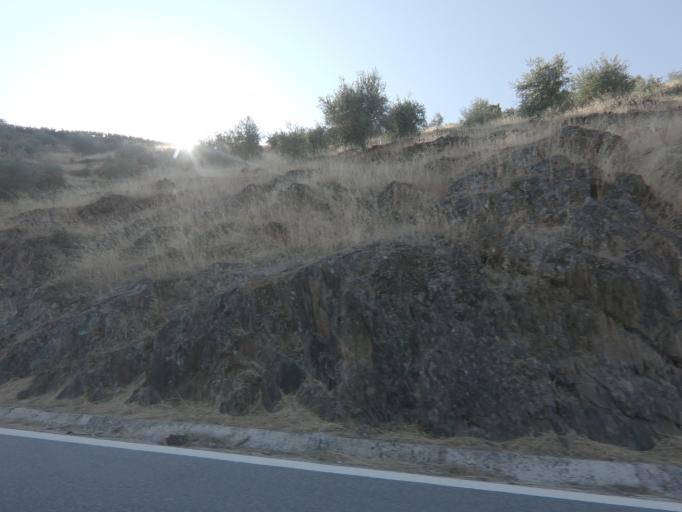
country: PT
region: Viseu
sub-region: Tabuaco
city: Tabuaco
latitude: 41.1376
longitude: -7.5652
